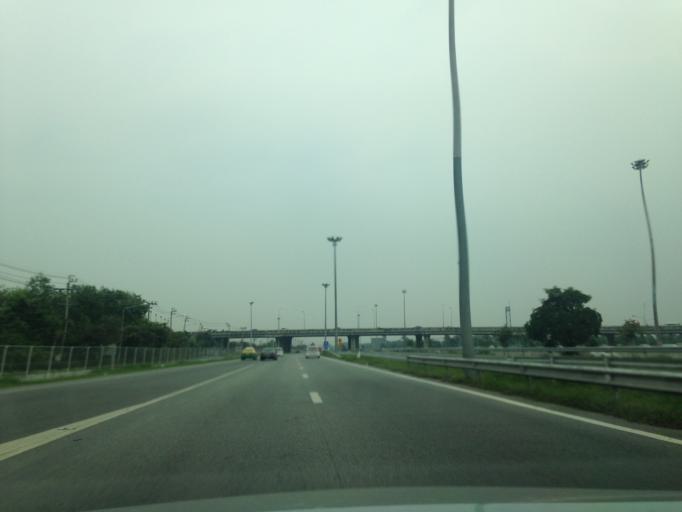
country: TH
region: Bangkok
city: Khan Na Yao
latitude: 13.8213
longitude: 100.6757
